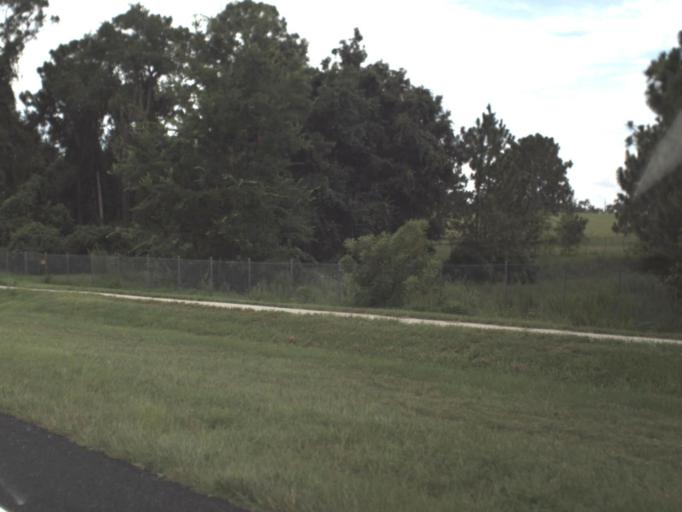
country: US
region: Florida
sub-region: Citrus County
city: Lecanto
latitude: 28.8715
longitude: -82.5160
